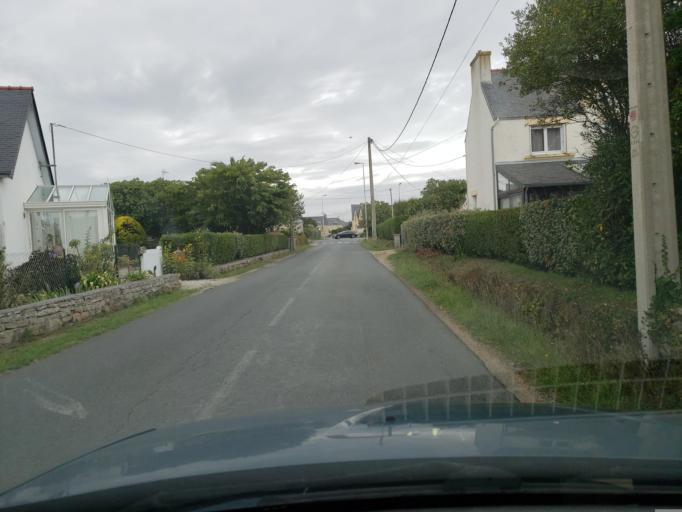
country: FR
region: Brittany
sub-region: Departement du Finistere
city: Plomeur
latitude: 47.8166
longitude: -4.3618
